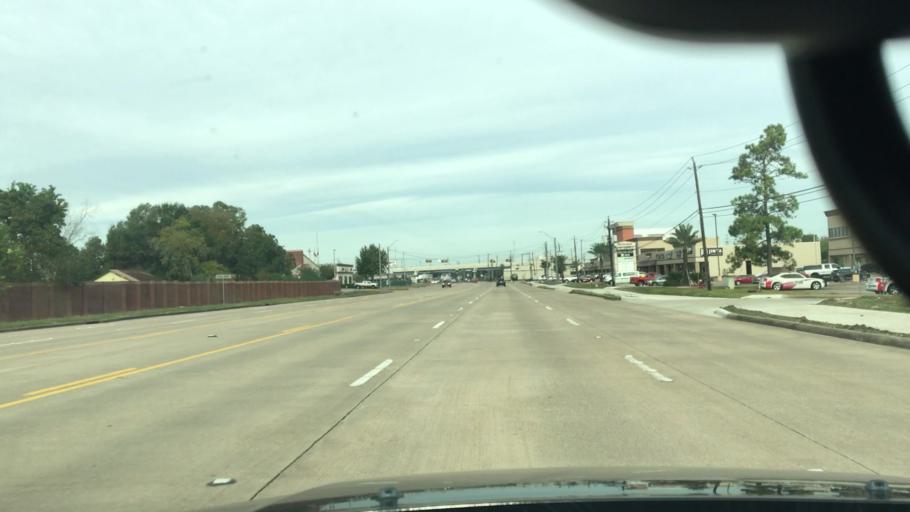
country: US
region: Texas
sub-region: Harris County
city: Nassau Bay
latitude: 29.5426
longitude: -95.1030
